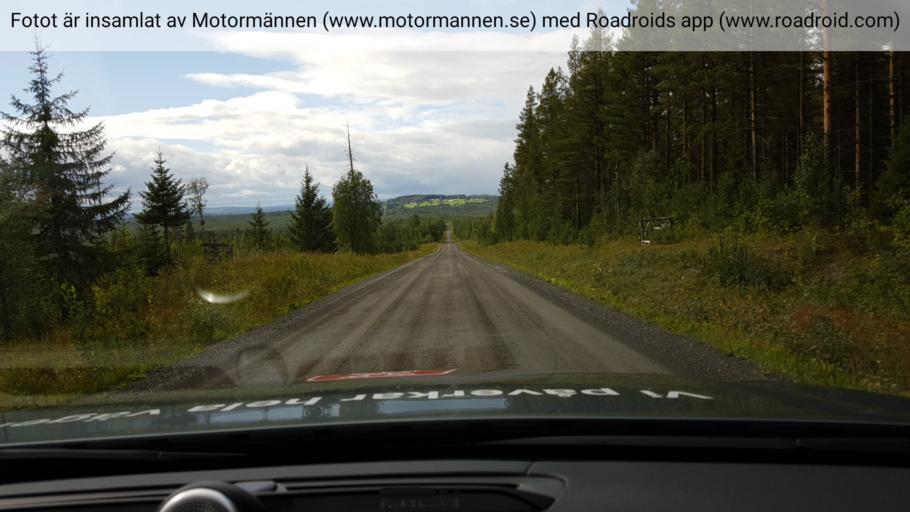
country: SE
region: Jaemtland
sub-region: OEstersunds Kommun
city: Lit
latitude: 63.6790
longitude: 14.8002
